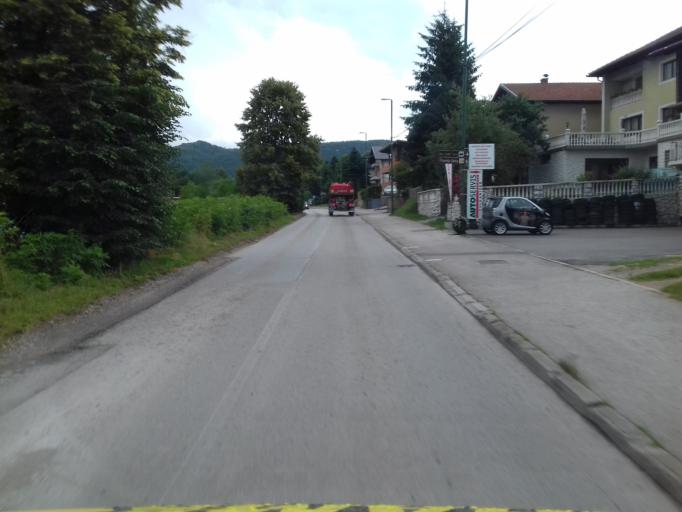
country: BA
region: Federation of Bosnia and Herzegovina
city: Visoko
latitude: 43.9797
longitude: 18.1844
